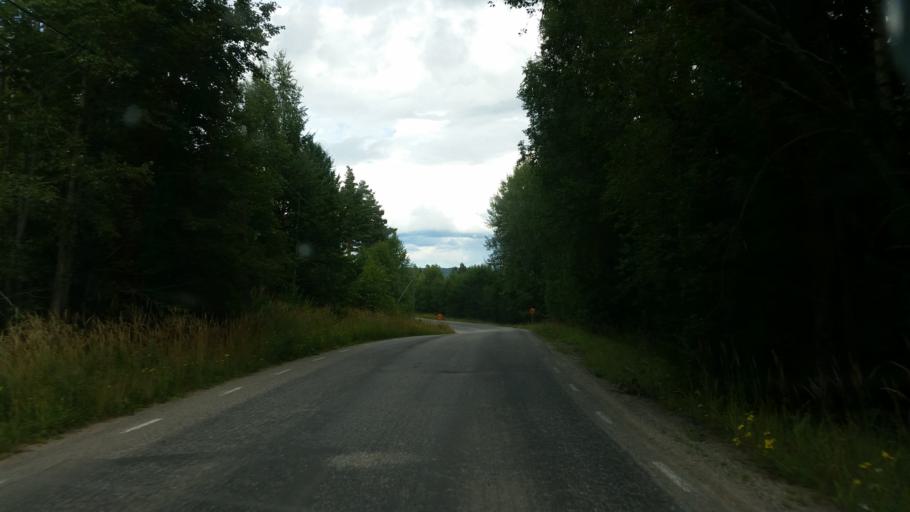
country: SE
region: Gaevleborg
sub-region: Hudiksvalls Kommun
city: Delsbo
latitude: 61.9169
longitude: 16.5961
